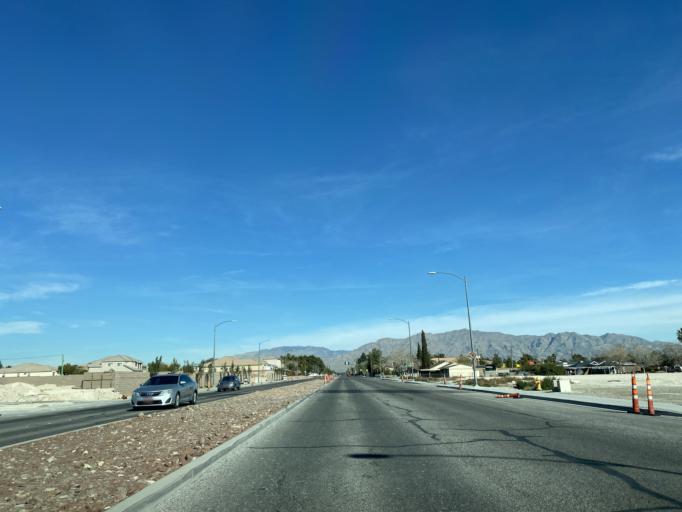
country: US
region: Nevada
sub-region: Clark County
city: Las Vegas
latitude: 36.2507
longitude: -115.2255
